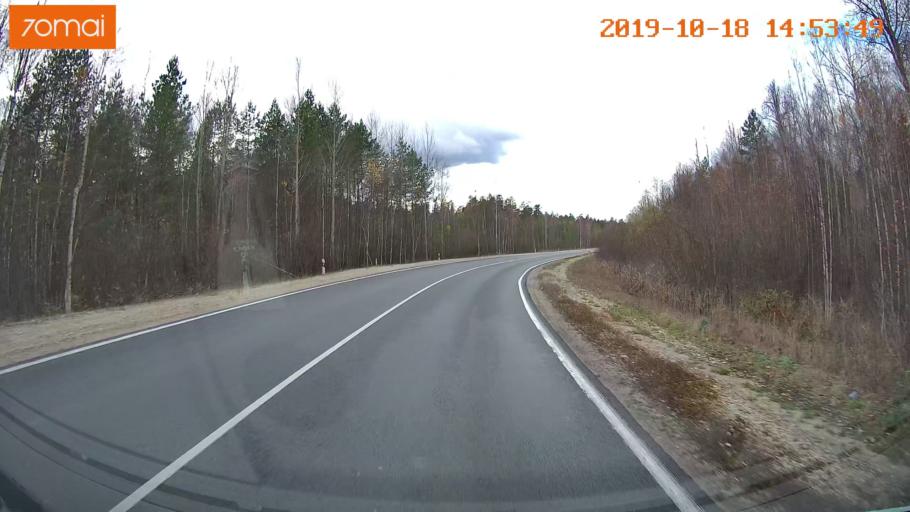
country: RU
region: Vladimir
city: Kurlovo
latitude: 55.4347
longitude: 40.6098
